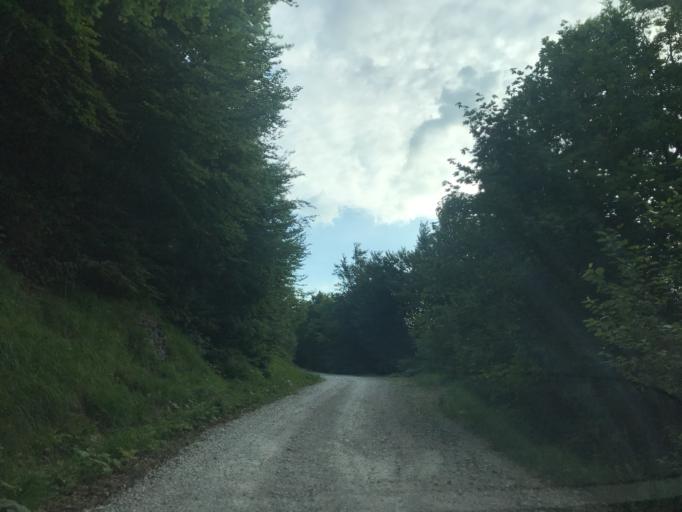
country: FR
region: Rhone-Alpes
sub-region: Departement de l'Isere
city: Saint-Vincent-de-Mercuze
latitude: 45.4129
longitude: 5.9357
